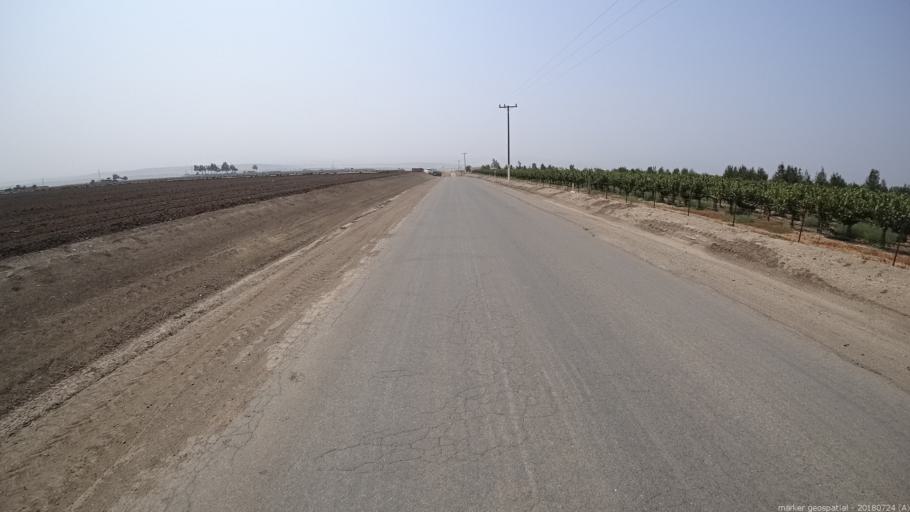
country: US
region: California
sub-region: Monterey County
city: King City
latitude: 36.1927
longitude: -121.0647
